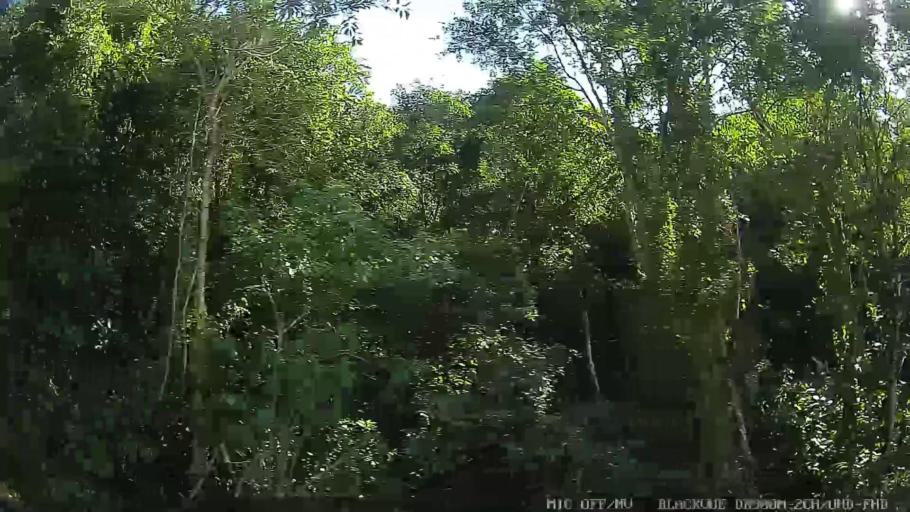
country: BR
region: Sao Paulo
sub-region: Santos
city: Santos
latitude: -23.9977
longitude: -46.3095
